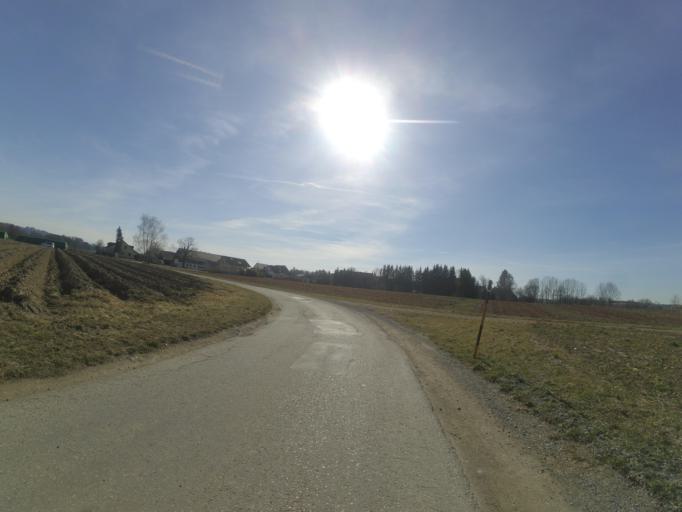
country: DE
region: Baden-Wuerttemberg
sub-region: Tuebingen Region
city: Ravensburg
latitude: 47.7493
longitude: 9.5892
